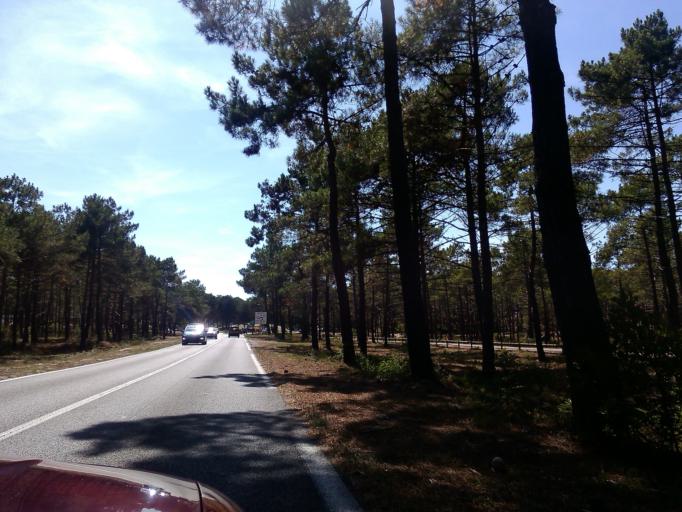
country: FR
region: Aquitaine
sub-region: Departement de la Gironde
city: Lacanau
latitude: 45.0052
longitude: -1.1796
